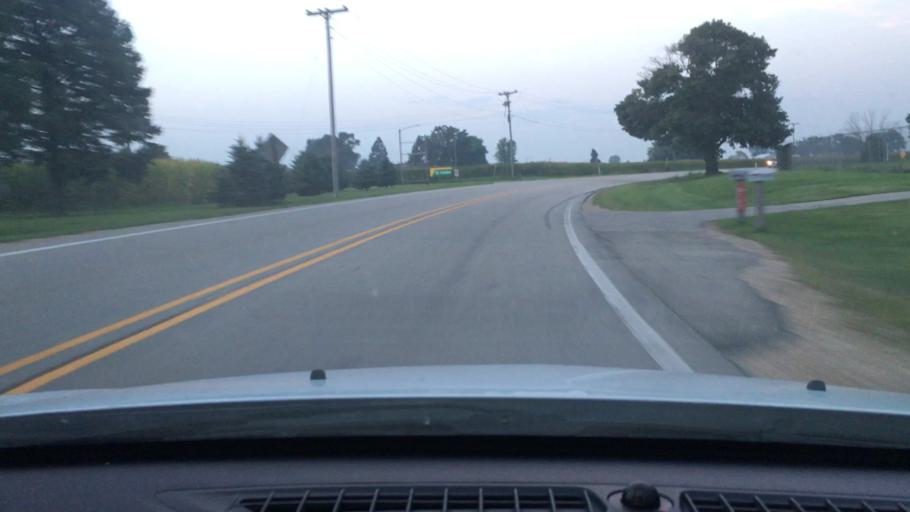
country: US
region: Illinois
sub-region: Ogle County
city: Rochelle
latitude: 41.8940
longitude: -89.0684
